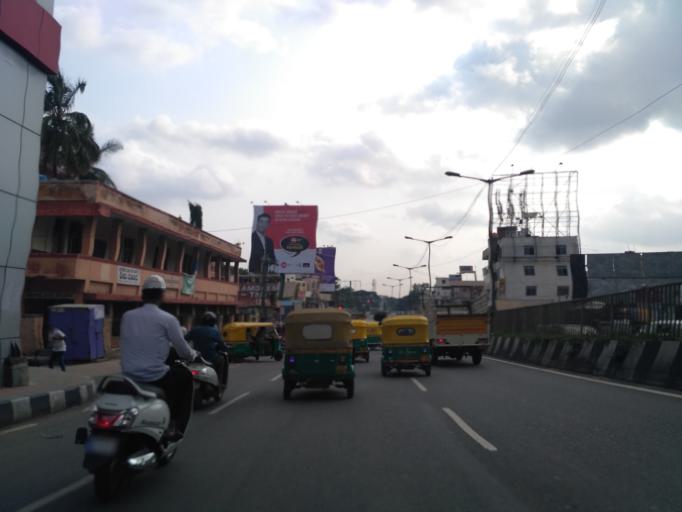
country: IN
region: Karnataka
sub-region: Bangalore Urban
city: Bangalore
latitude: 12.9579
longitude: 77.5538
